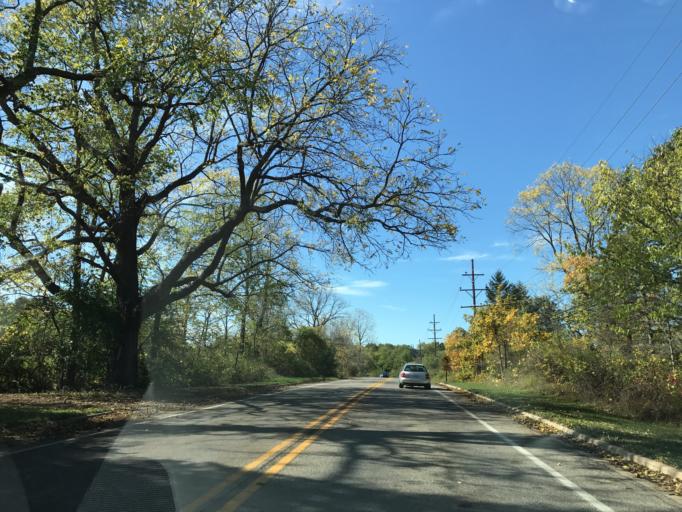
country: US
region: Michigan
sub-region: Washtenaw County
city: Ypsilanti
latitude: 42.2681
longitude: -83.6717
